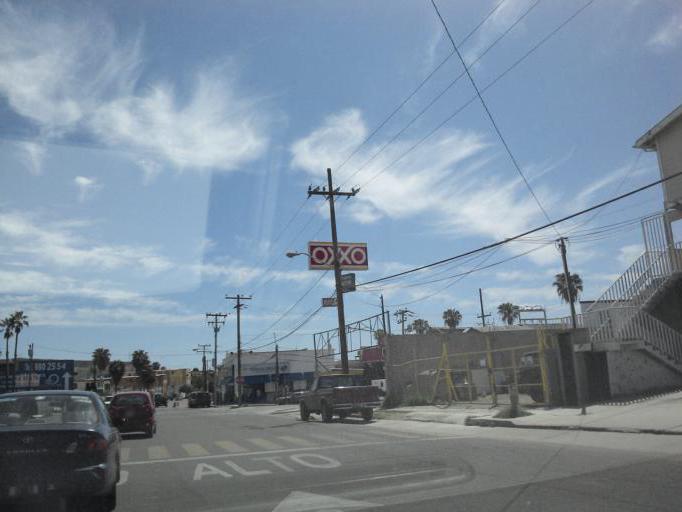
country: MX
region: Baja California
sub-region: Tijuana
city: La Esperanza [Granjas Familiares]
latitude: 32.5121
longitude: -117.1201
